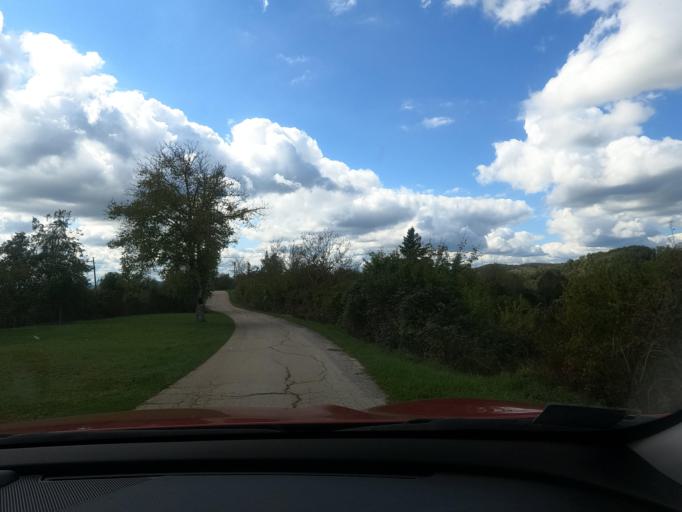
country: HR
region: Karlovacka
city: Vojnic
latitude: 45.2407
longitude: 15.7077
